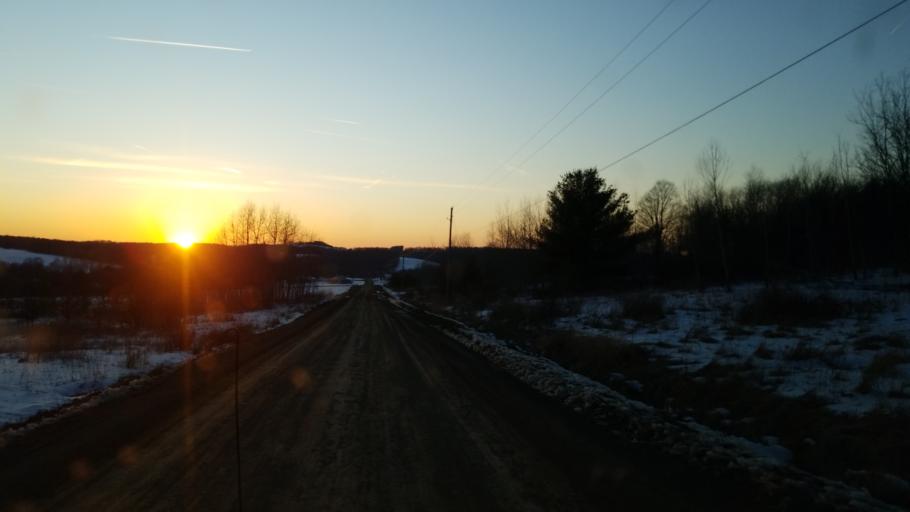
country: US
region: New York
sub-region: Allegany County
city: Andover
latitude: 42.0070
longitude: -77.7087
